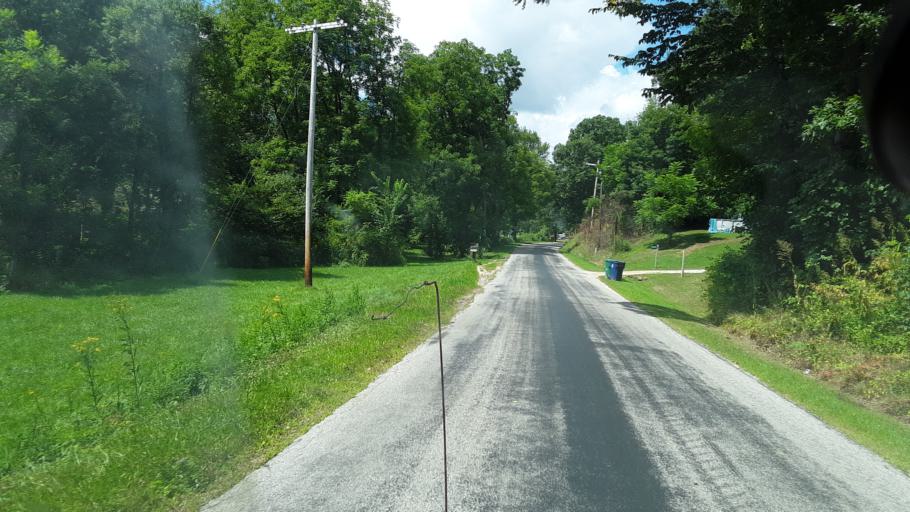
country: US
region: Ohio
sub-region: Licking County
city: Utica
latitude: 40.1997
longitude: -82.3194
